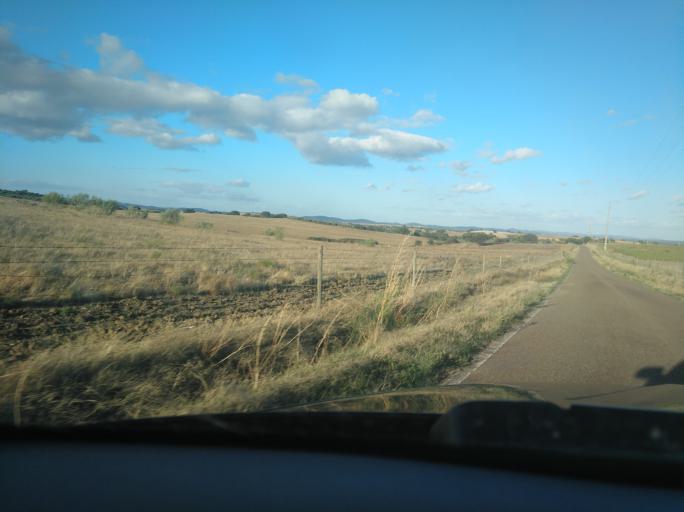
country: PT
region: Portalegre
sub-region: Campo Maior
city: Campo Maior
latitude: 39.0267
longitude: -7.0255
